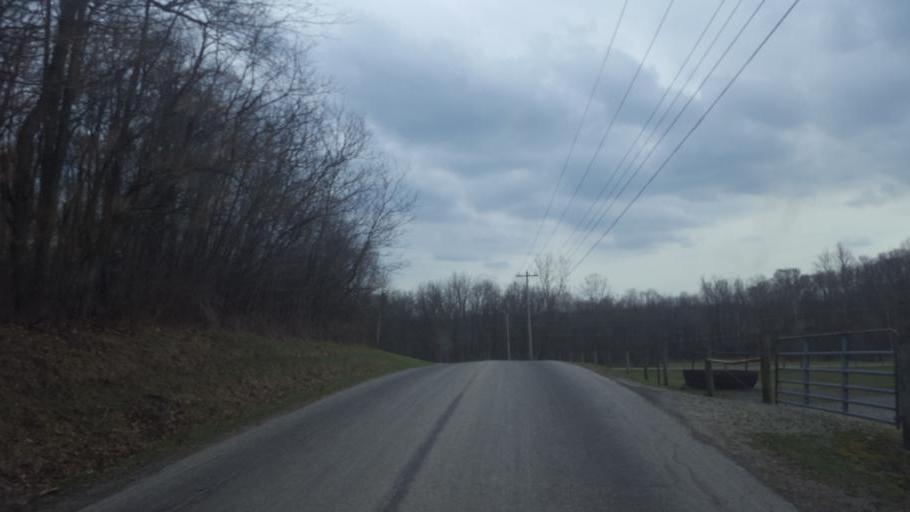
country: US
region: Ohio
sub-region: Knox County
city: Fredericktown
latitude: 40.5585
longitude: -82.6047
